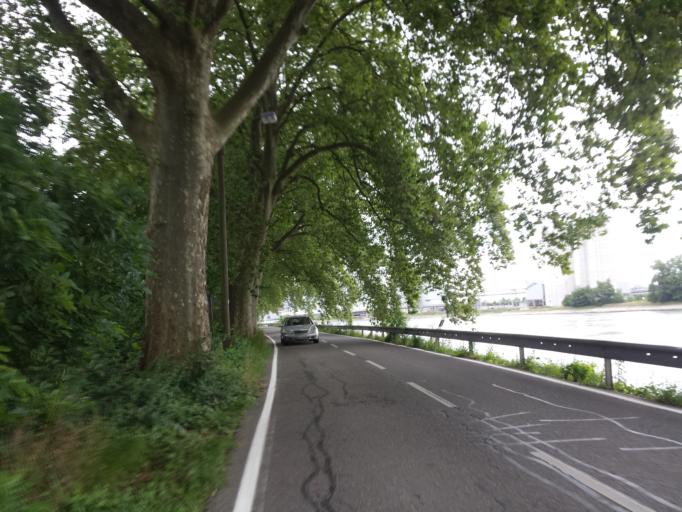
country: DE
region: Rheinland-Pfalz
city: Altrip
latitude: 49.4352
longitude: 8.5062
